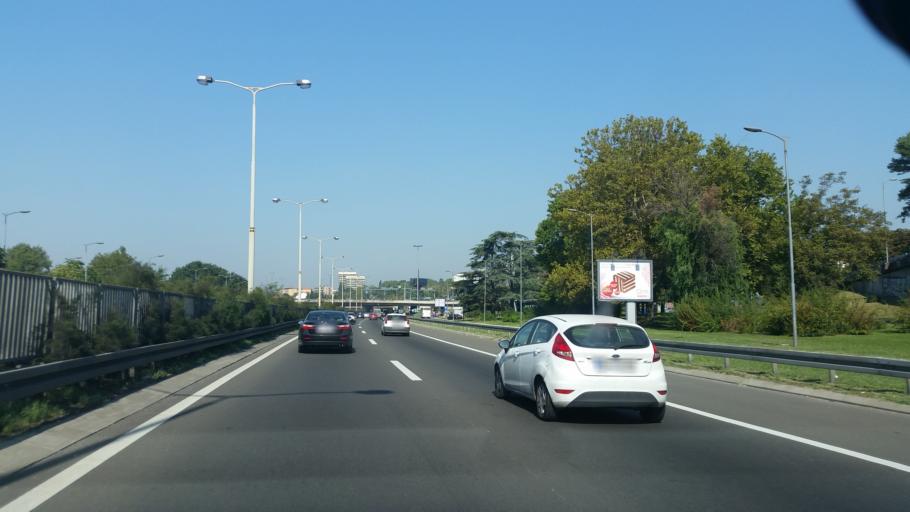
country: RS
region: Central Serbia
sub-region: Belgrade
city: Vracar
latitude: 44.7891
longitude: 20.4704
